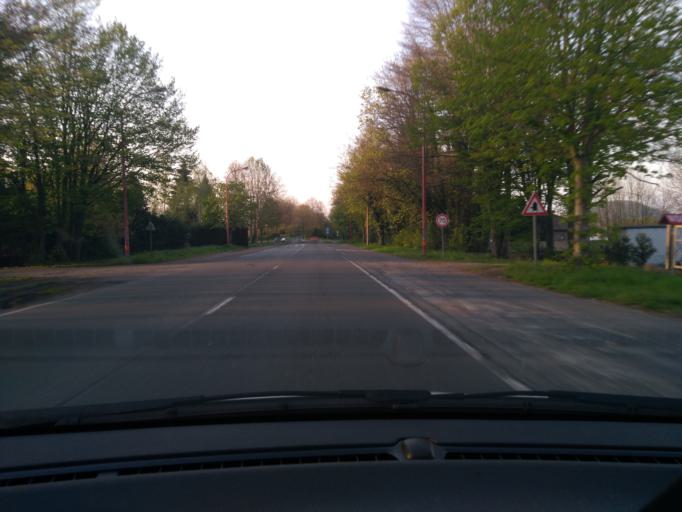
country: BE
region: Wallonia
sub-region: Province du Hainaut
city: Quaregnon
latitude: 50.4221
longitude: 3.8765
